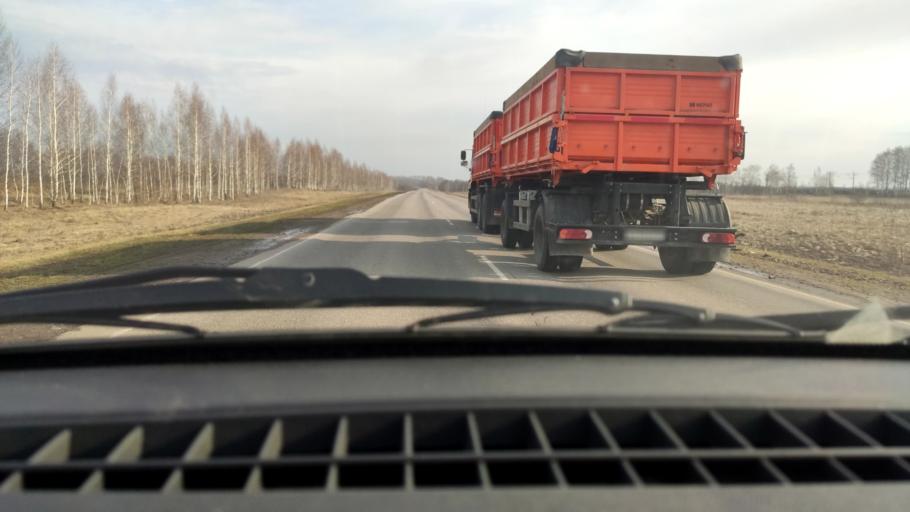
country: RU
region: Bashkortostan
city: Chishmy
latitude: 54.4359
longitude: 55.2365
